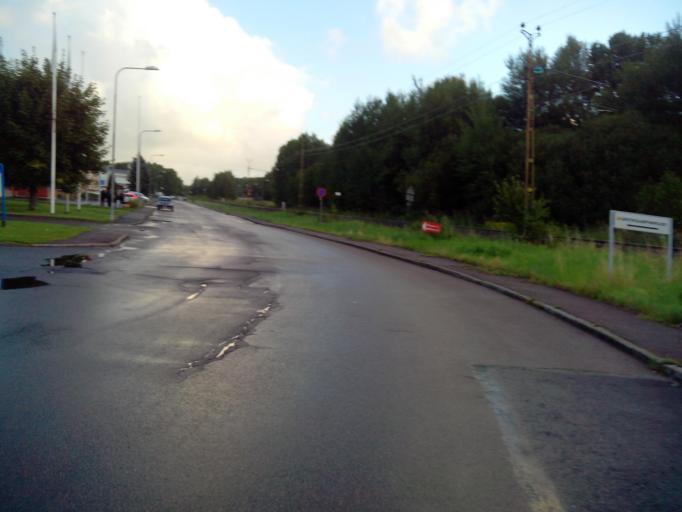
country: SE
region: Vaestra Goetaland
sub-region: Goteborg
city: Goeteborg
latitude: 57.7396
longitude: 11.9539
